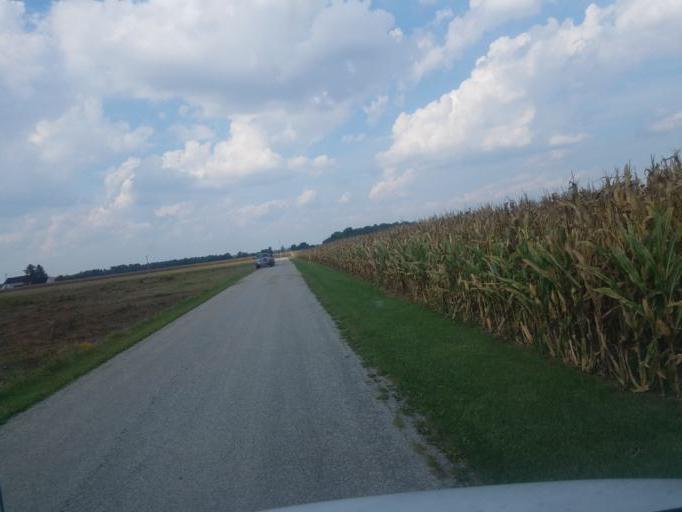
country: US
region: Ohio
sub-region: Hardin County
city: Kenton
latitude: 40.7292
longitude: -83.6145
